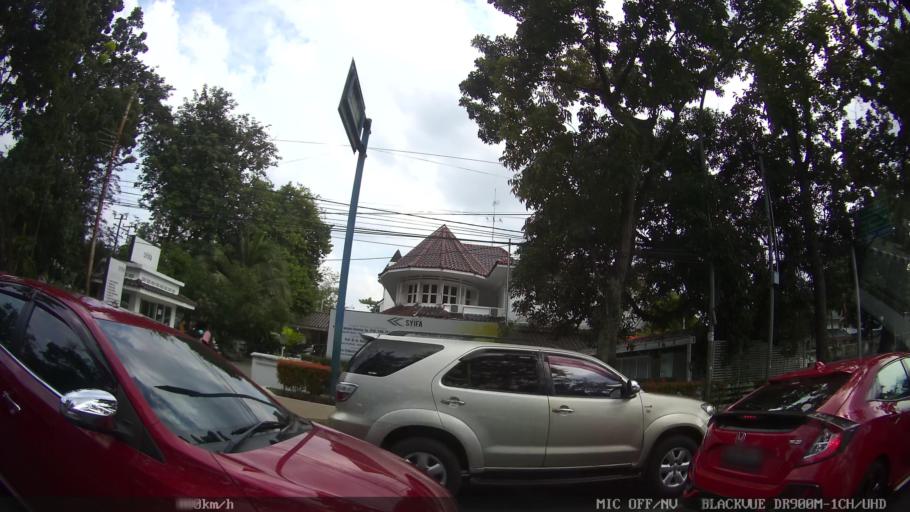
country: ID
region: North Sumatra
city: Medan
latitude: 3.5756
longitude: 98.6735
